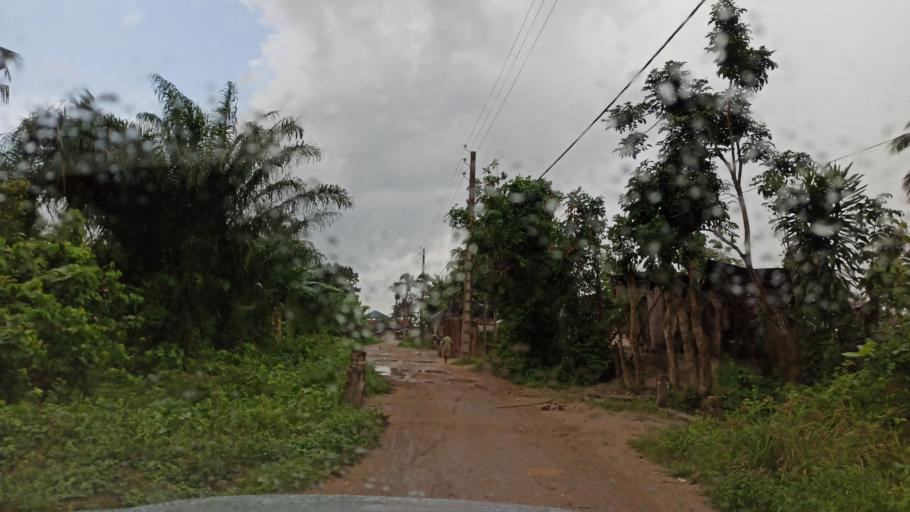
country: BJ
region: Queme
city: Porto-Novo
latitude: 6.4533
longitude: 2.6567
